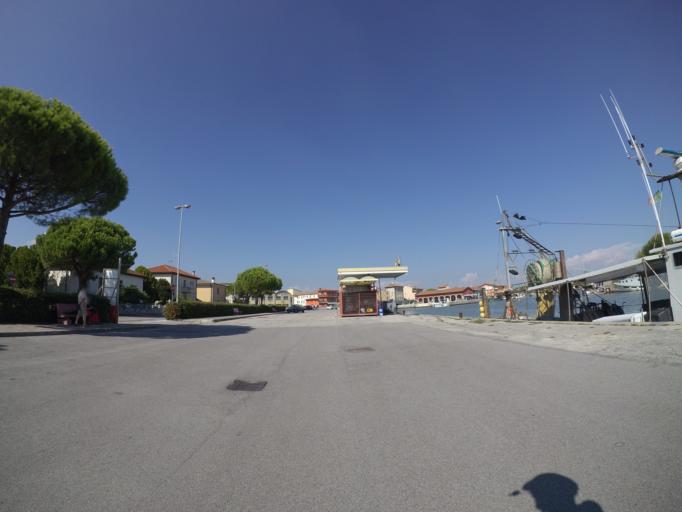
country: IT
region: Friuli Venezia Giulia
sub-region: Provincia di Udine
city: Marano Lagunare
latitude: 45.7616
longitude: 13.1659
